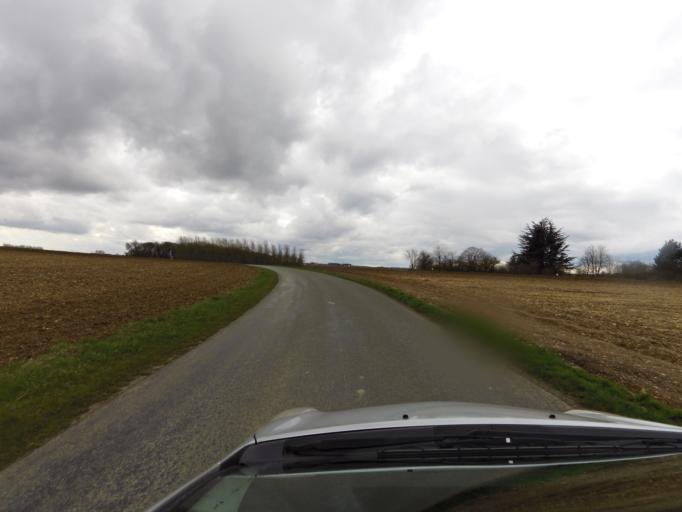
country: FR
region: Picardie
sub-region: Departement de la Somme
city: Bray-sur-Somme
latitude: 49.9303
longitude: 2.8098
